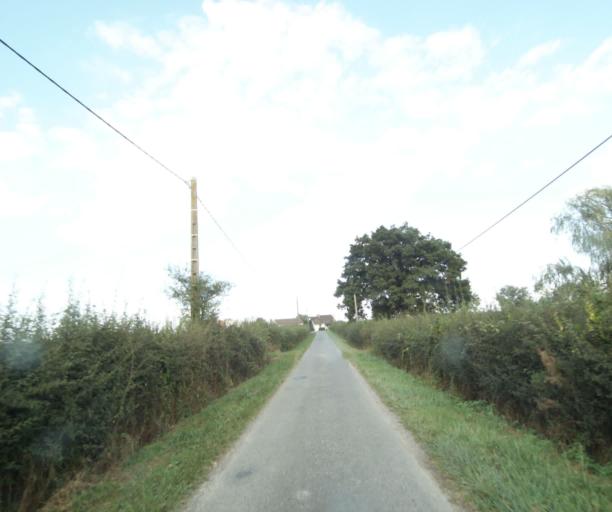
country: FR
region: Bourgogne
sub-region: Departement de Saone-et-Loire
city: Palinges
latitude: 46.5620
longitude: 4.1872
